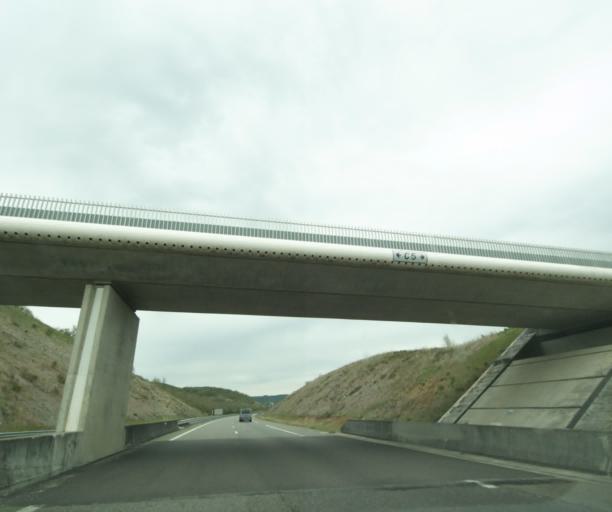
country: FR
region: Midi-Pyrenees
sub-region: Departement du Lot
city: Cahors
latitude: 44.4348
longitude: 1.5036
